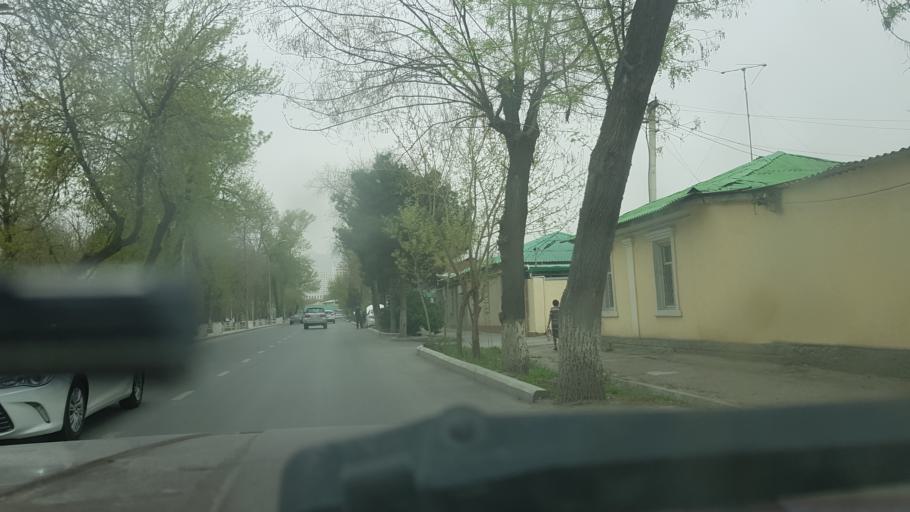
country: TM
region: Ahal
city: Ashgabat
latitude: 37.9514
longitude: 58.3629
